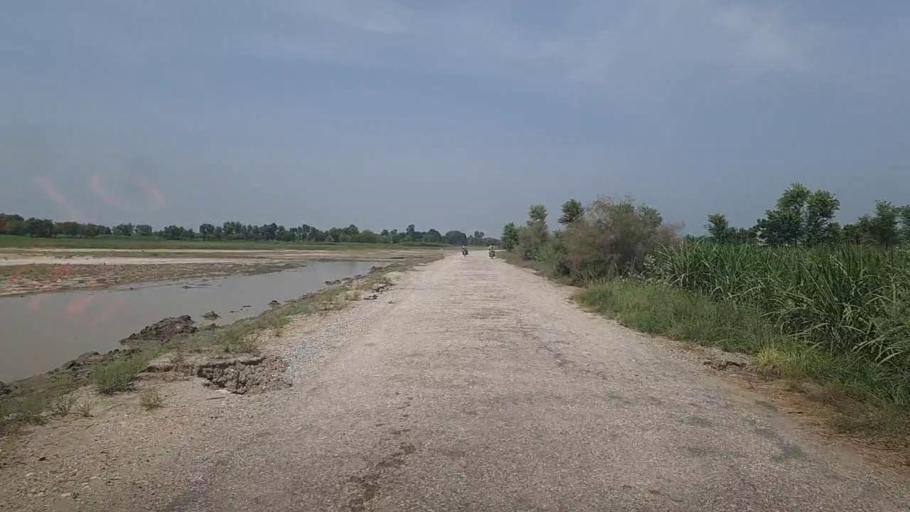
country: PK
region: Sindh
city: Ubauro
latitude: 28.1854
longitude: 69.7694
